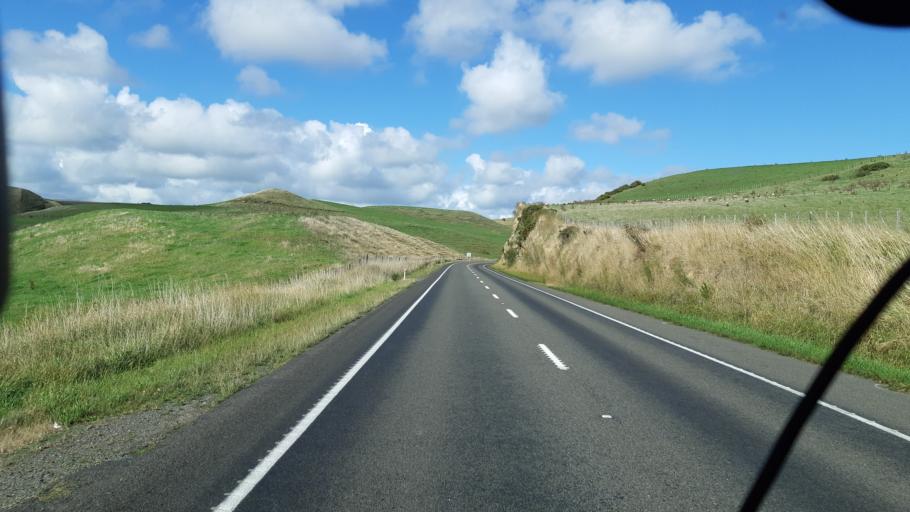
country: NZ
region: Manawatu-Wanganui
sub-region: Wanganui District
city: Wanganui
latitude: -40.0173
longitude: 175.1750
